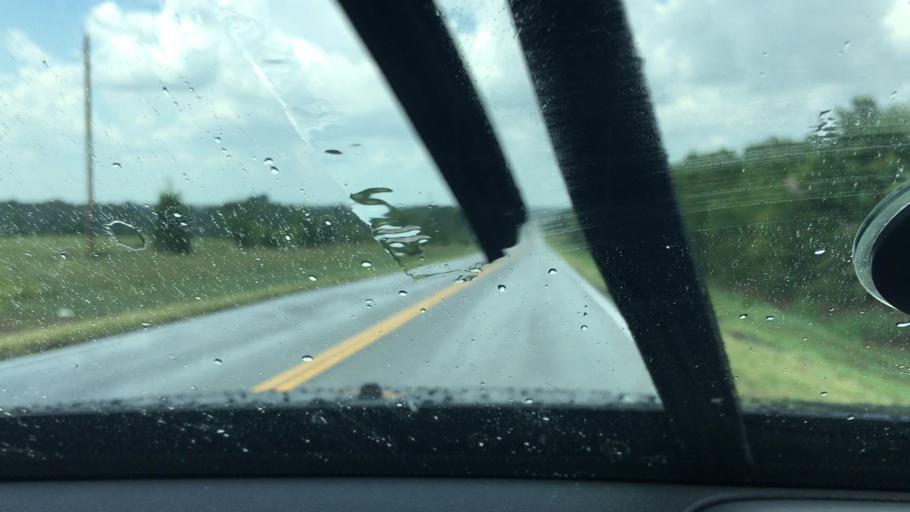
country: US
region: Oklahoma
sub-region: Johnston County
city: Tishomingo
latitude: 34.1903
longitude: -96.7232
